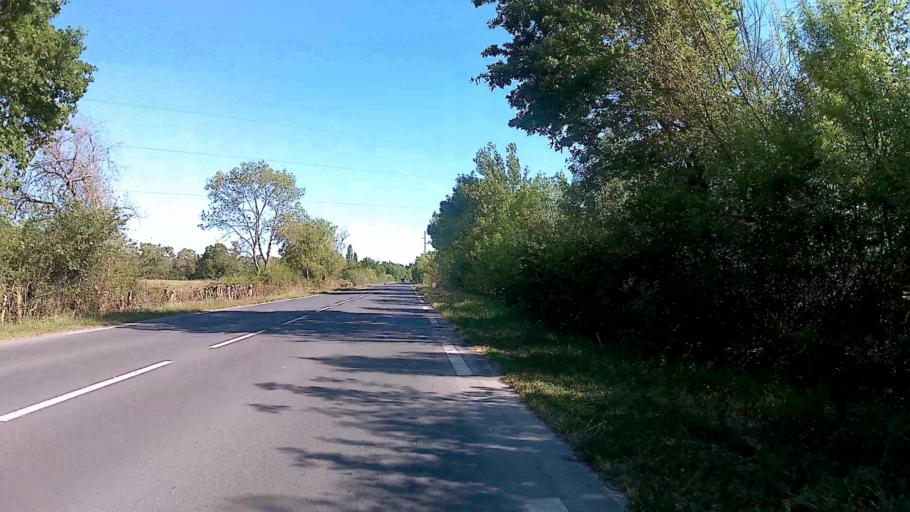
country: FR
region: Aquitaine
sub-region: Departement de la Gironde
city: Cadaujac
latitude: 44.7668
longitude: -0.5286
